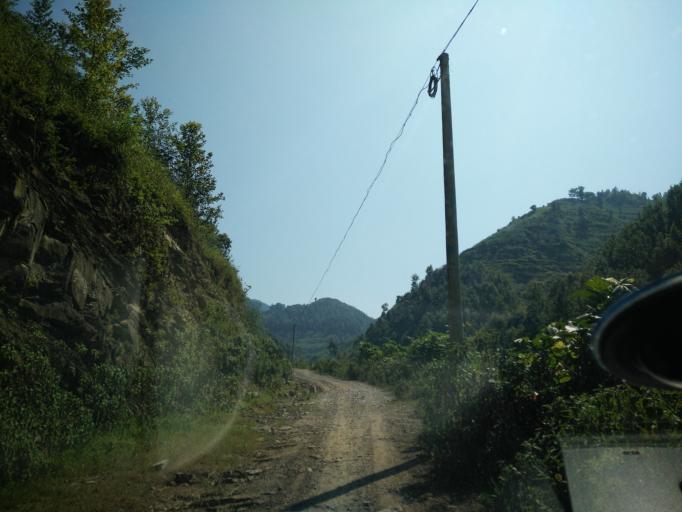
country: CN
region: Guangxi Zhuangzu Zizhiqu
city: Xinzhou
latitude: 25.1819
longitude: 105.6870
